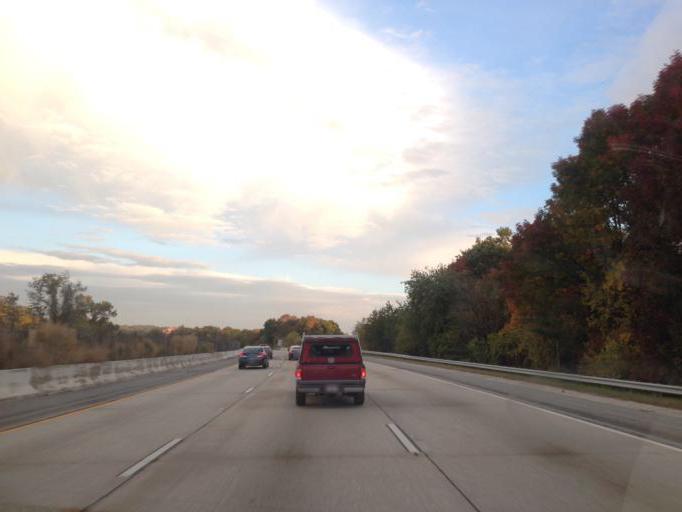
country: US
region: Maryland
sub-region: Baltimore County
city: Garrison
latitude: 39.4012
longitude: -76.7647
